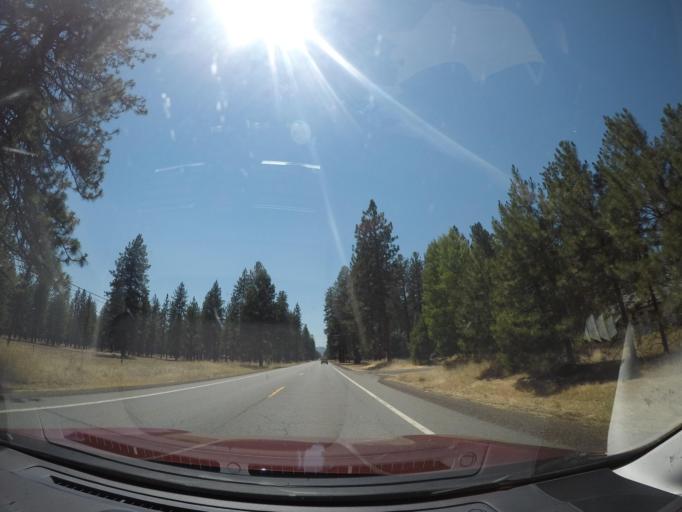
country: US
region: California
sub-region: Shasta County
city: Burney
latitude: 41.0618
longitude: -121.3669
